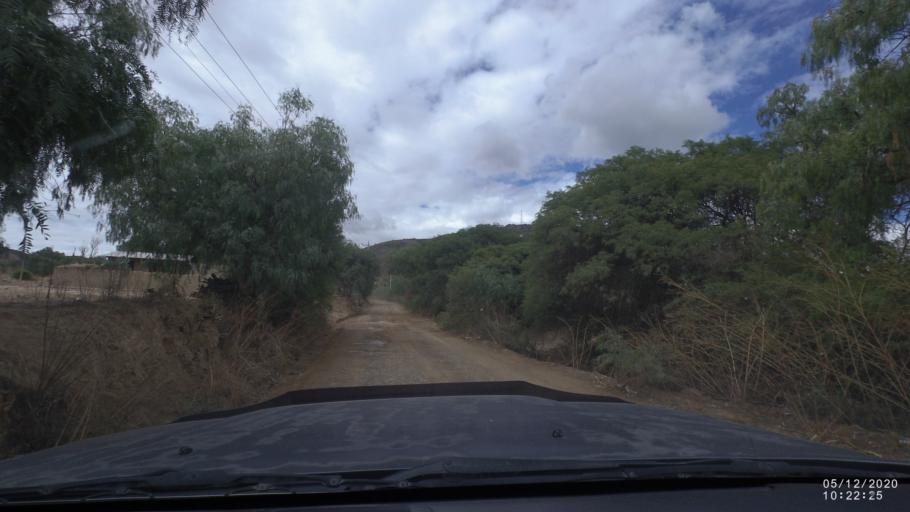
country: BO
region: Cochabamba
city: Sipe Sipe
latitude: -17.4959
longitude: -66.2823
